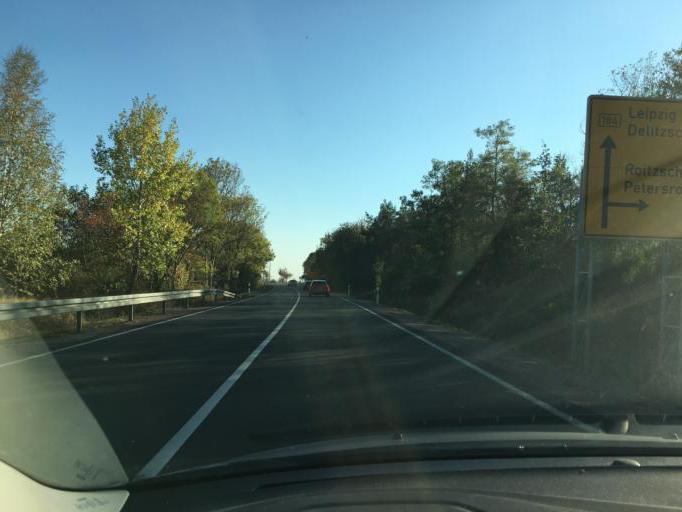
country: DE
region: Saxony-Anhalt
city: Roitzsch
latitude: 51.5712
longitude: 12.2842
